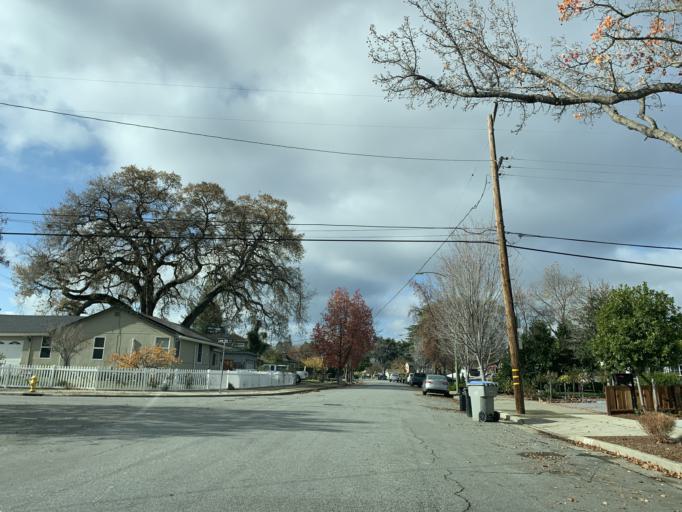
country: US
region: California
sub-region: Santa Clara County
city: Cambrian Park
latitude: 37.2470
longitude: -121.9209
